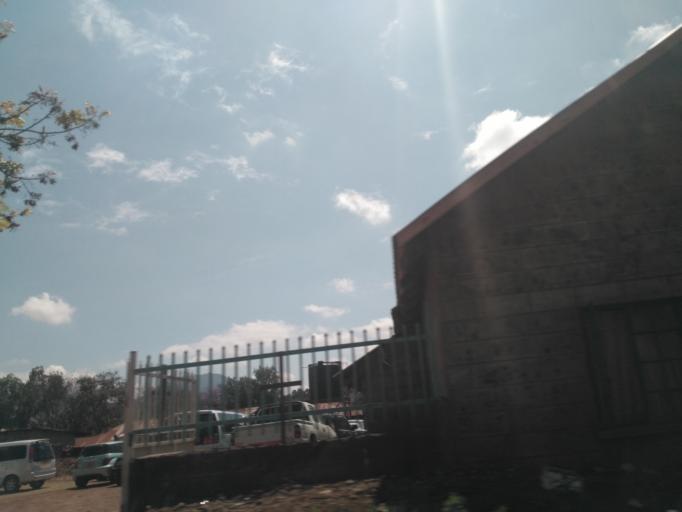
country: TZ
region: Arusha
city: Arusha
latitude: -3.3680
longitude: 36.6879
